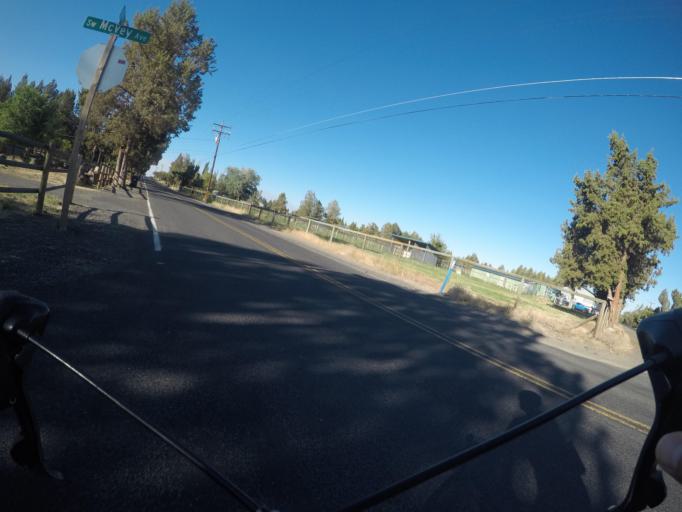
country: US
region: Oregon
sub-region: Deschutes County
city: Redmond
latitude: 44.2185
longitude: -121.2434
